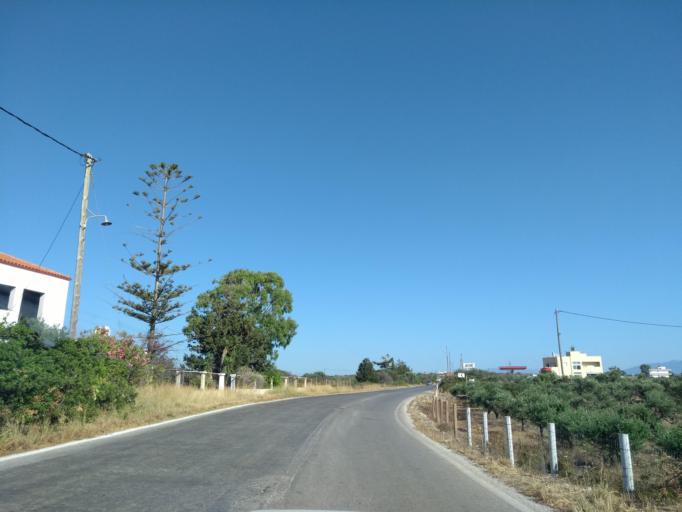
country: GR
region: Crete
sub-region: Nomos Chanias
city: Pithari
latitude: 35.5823
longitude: 24.0918
